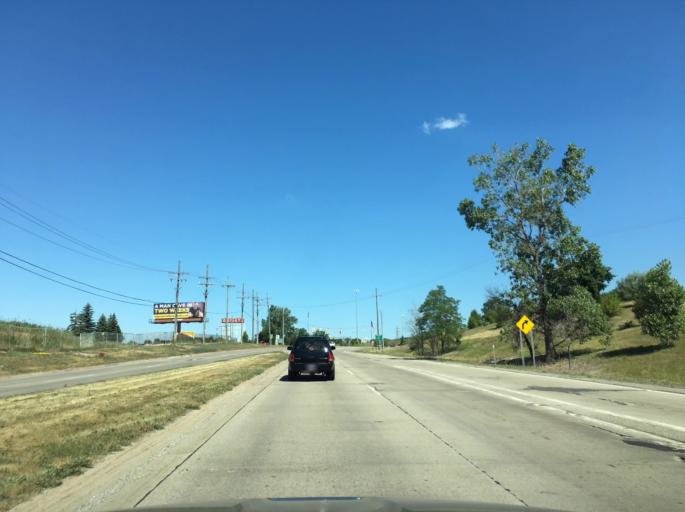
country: US
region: Michigan
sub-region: Oakland County
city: Auburn Hills
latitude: 42.6984
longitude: -83.2818
